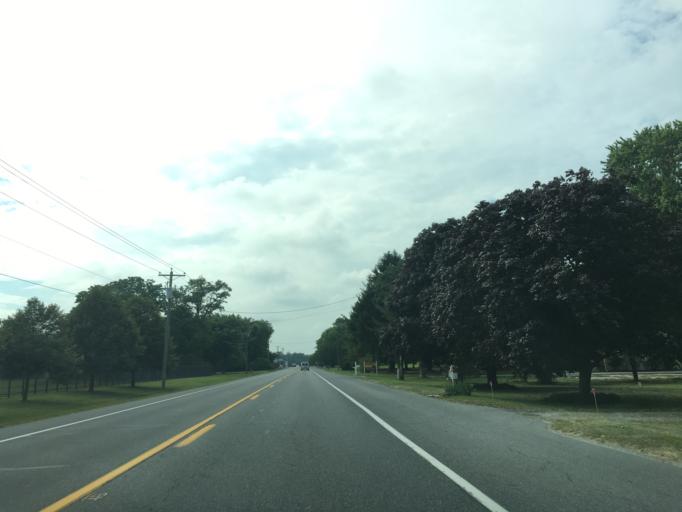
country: US
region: Delaware
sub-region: Sussex County
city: Long Neck
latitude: 38.5543
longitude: -75.1944
